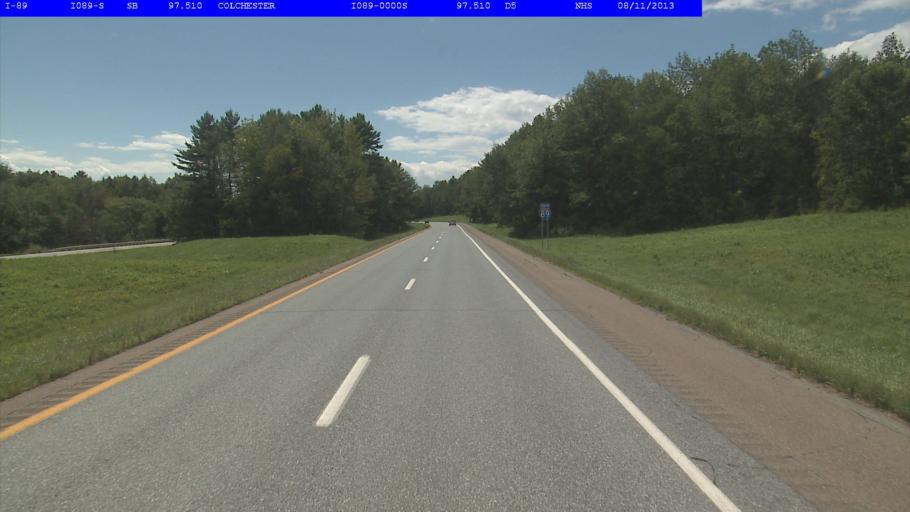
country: US
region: Vermont
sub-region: Chittenden County
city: Colchester
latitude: 44.5851
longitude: -73.1732
